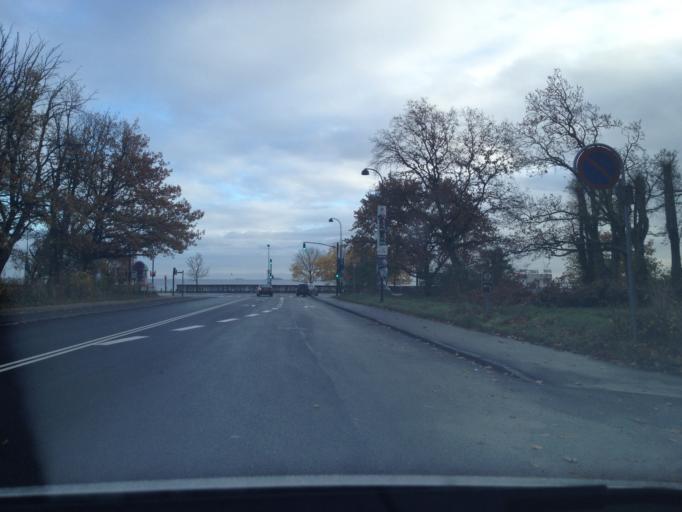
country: DK
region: Capital Region
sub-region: Gentofte Kommune
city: Charlottenlund
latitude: 55.7489
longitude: 12.5860
